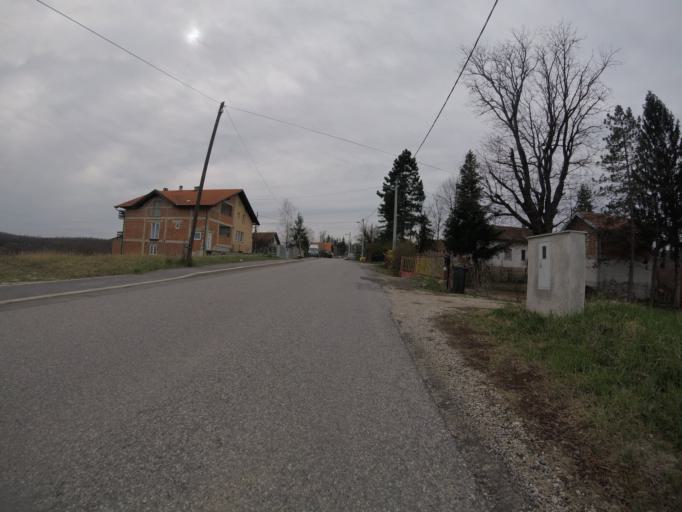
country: HR
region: Grad Zagreb
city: Strmec
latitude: 45.6418
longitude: 15.9353
